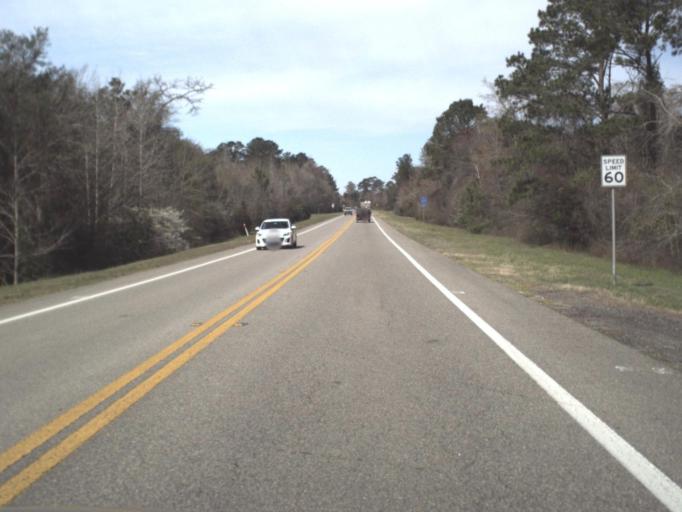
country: US
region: Florida
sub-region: Gadsden County
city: Quincy
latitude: 30.3854
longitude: -84.6542
